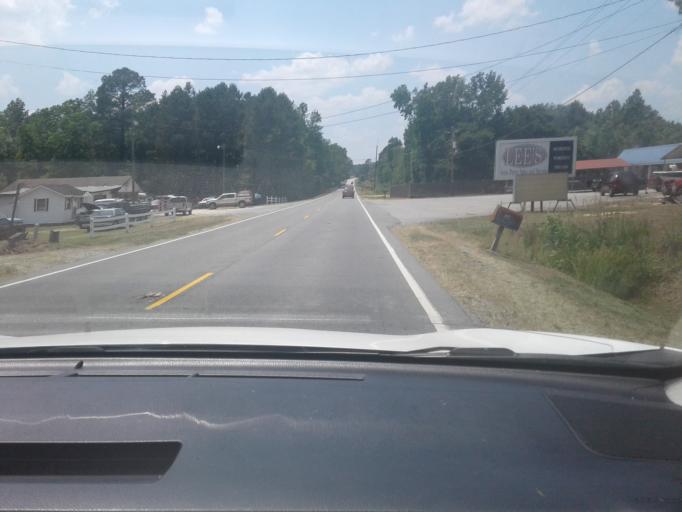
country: US
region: North Carolina
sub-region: Johnston County
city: Benson
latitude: 35.3887
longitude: -78.5719
